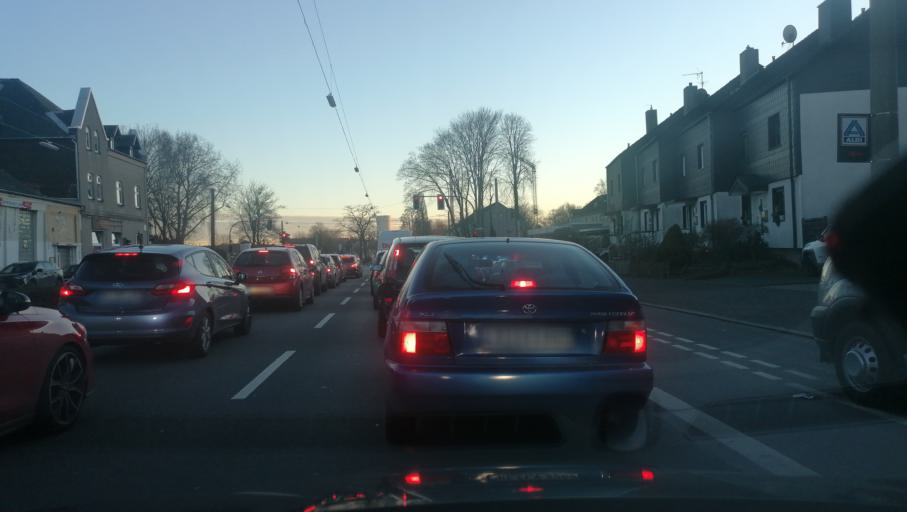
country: DE
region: North Rhine-Westphalia
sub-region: Regierungsbezirk Munster
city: Recklinghausen
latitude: 51.5735
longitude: 7.1852
